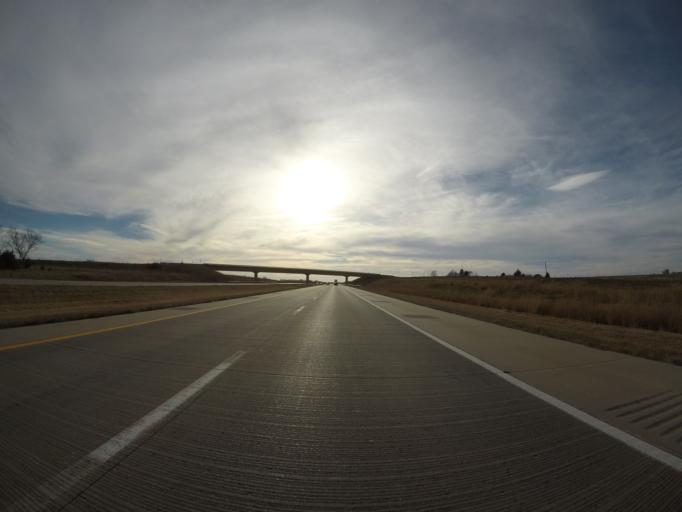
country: US
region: Kansas
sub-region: Franklin County
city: Ottawa
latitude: 38.6531
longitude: -95.1943
